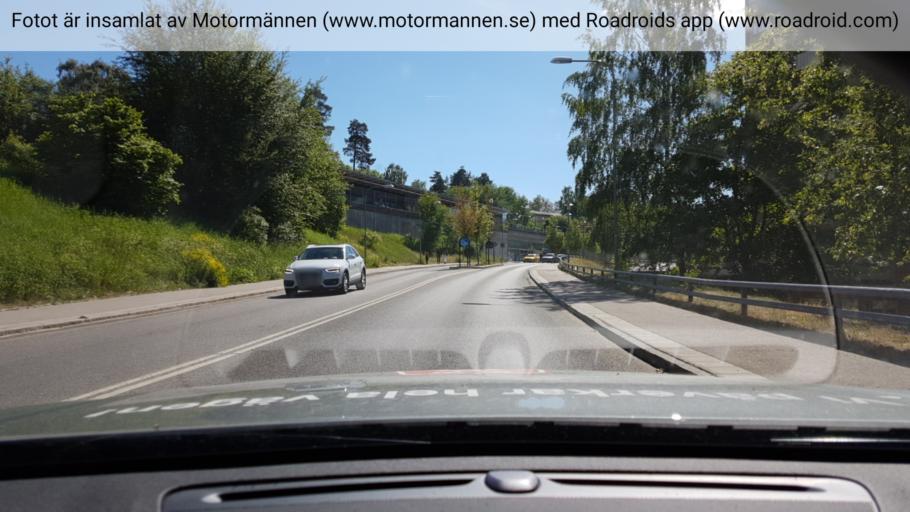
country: SE
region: Stockholm
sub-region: Stockholms Kommun
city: Arsta
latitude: 59.2577
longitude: 18.0295
